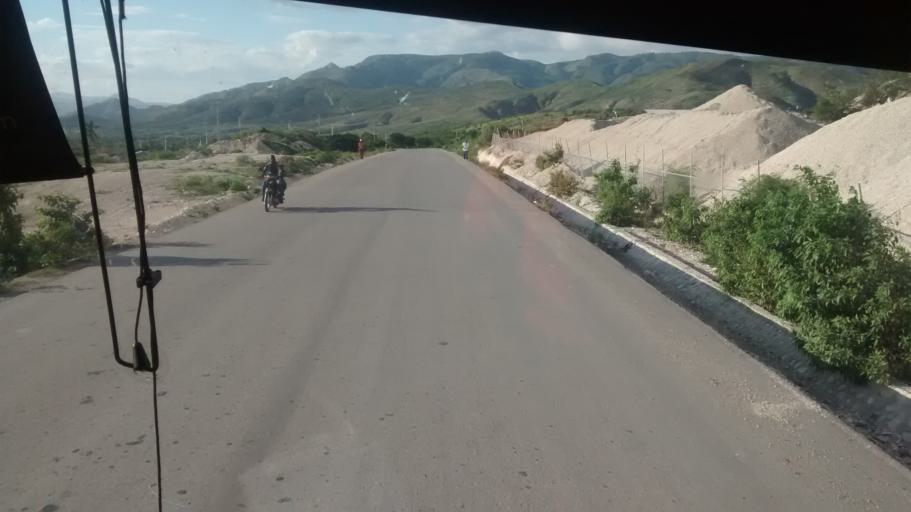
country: HT
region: Artibonite
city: Ennery
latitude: 19.5168
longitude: -72.5580
